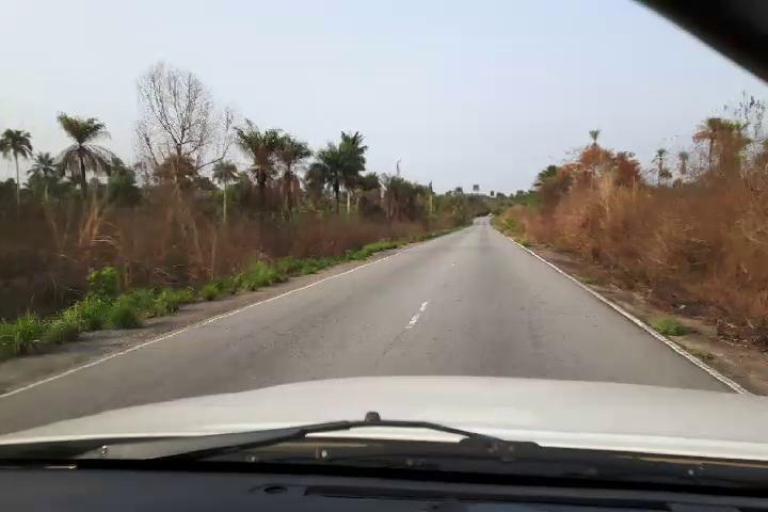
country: SL
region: Eastern Province
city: Blama
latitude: 7.9403
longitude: -11.5064
